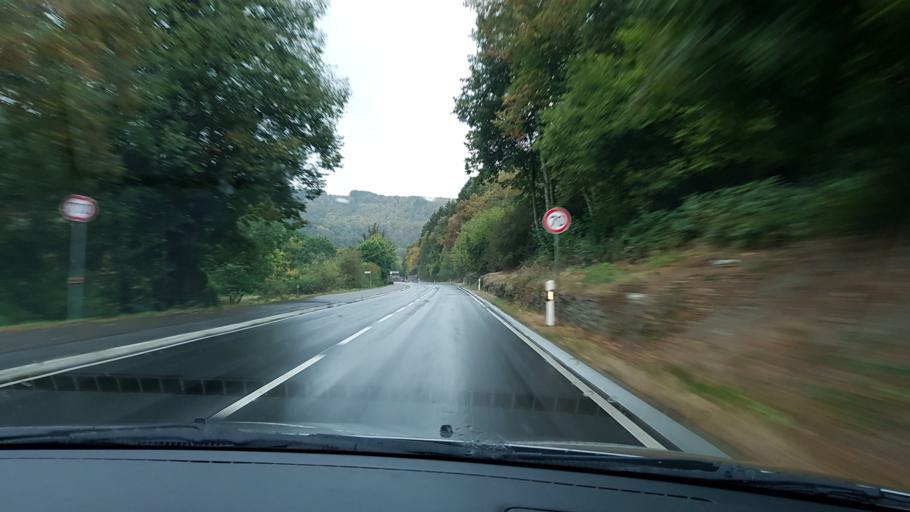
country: DE
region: Rheinland-Pfalz
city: Sulzbach
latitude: 50.3223
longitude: 7.7436
